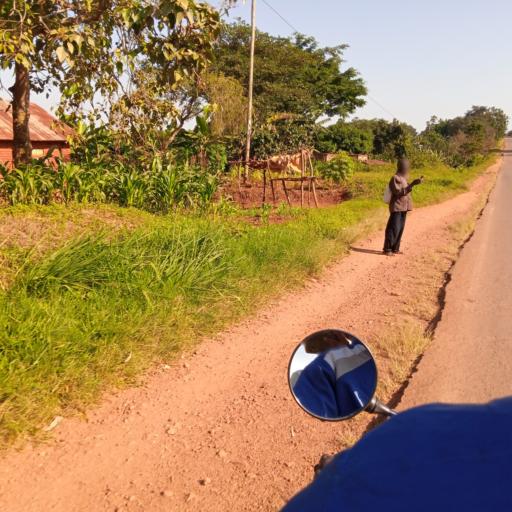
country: UG
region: Central Region
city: Masaka
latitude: -0.4416
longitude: 31.6650
